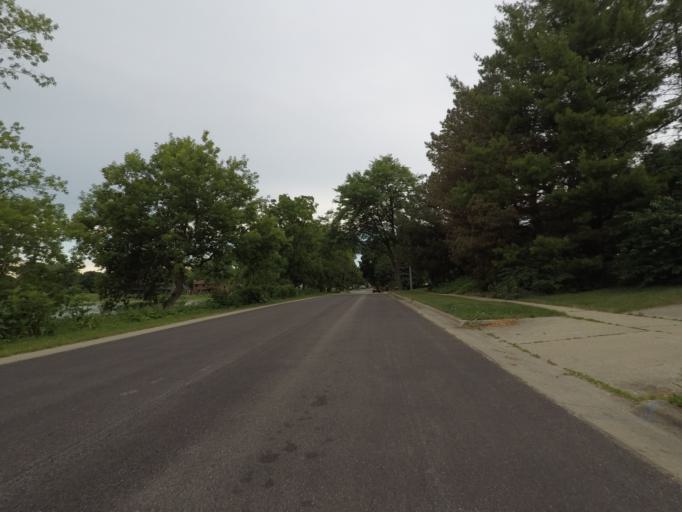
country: US
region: Wisconsin
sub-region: Dane County
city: Middleton
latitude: 43.0875
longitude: -89.5078
